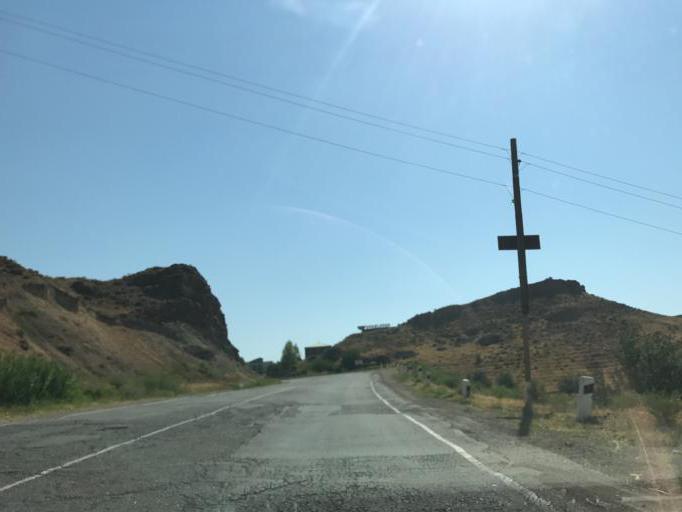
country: AM
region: Vayots' Dzori Marz
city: Yeghegnadzor
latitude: 39.7520
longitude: 45.3255
